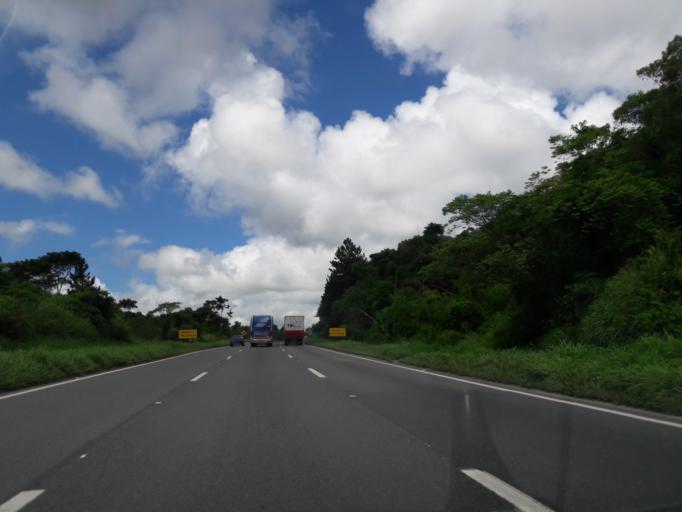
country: BR
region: Sao Paulo
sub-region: Cajati
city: Cajati
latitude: -24.9794
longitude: -48.5058
